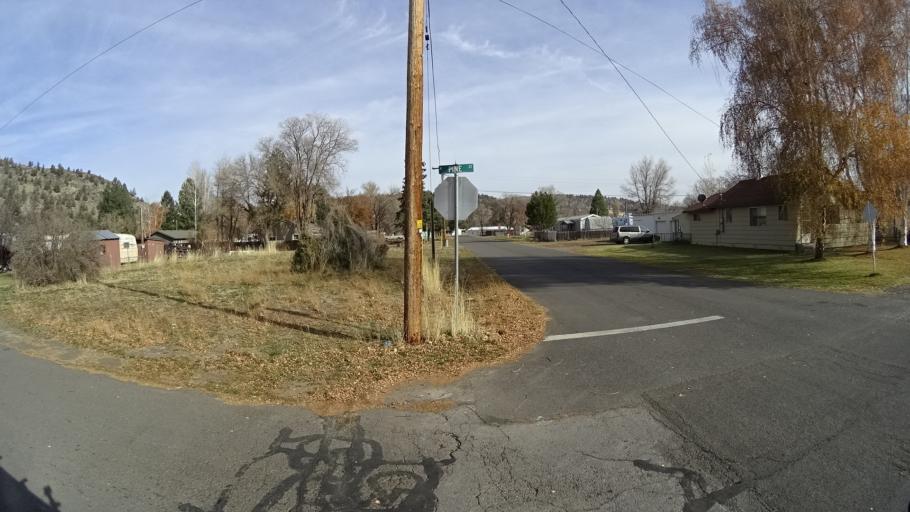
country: US
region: Oregon
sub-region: Klamath County
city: Klamath Falls
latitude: 41.9686
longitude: -121.9172
